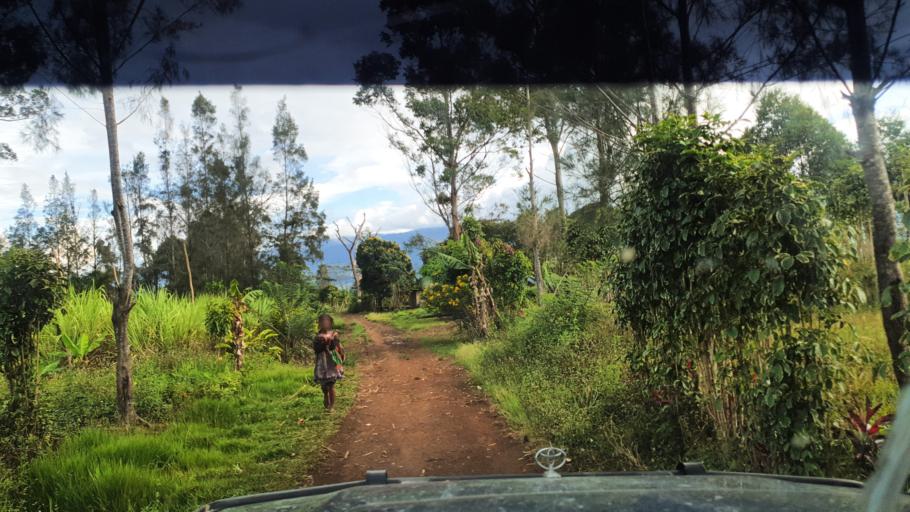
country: PG
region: Jiwaka
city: Minj
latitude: -5.9137
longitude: 144.8202
